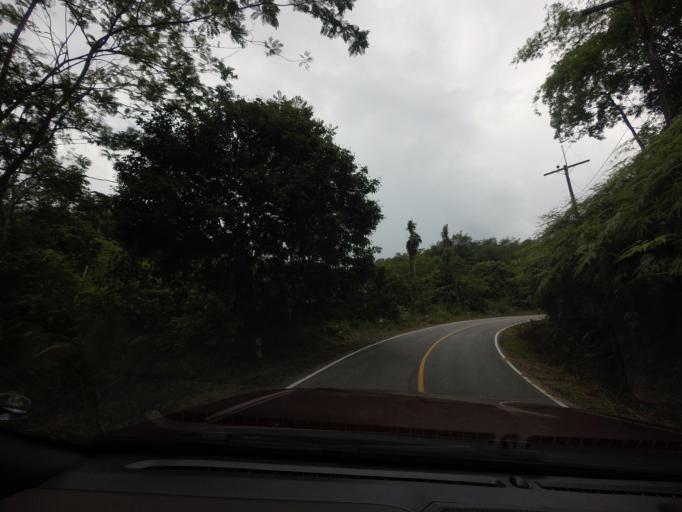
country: TH
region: Narathiwat
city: Sukhirin
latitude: 5.9813
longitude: 101.6826
